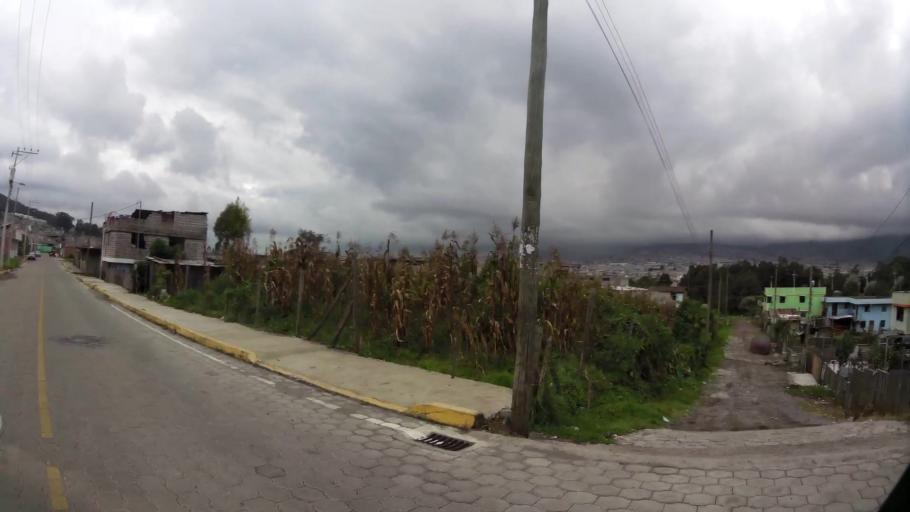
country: EC
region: Pichincha
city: Sangolqui
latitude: -0.3240
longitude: -78.5324
